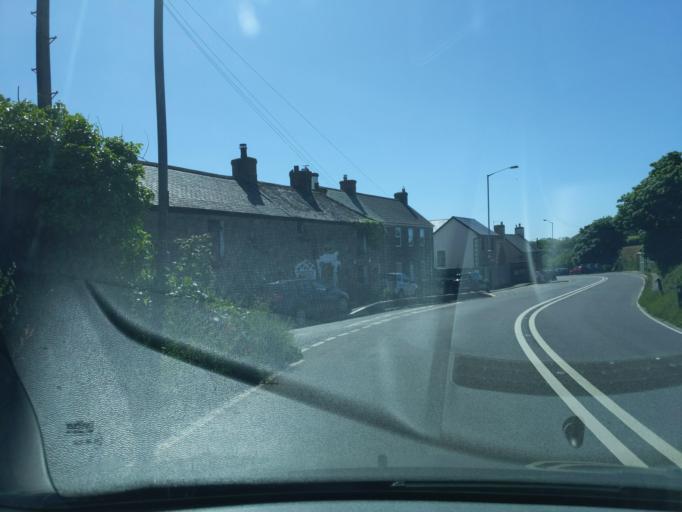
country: GB
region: England
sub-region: Cornwall
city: Wendron
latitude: 50.1132
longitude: -5.2469
